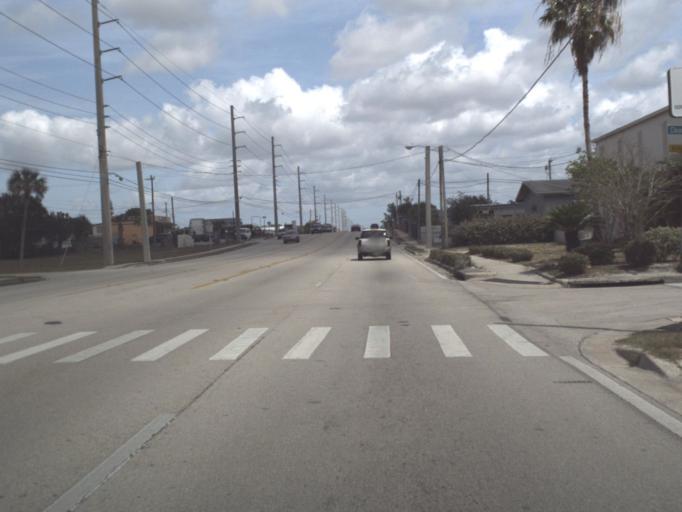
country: US
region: Florida
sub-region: Brevard County
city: Cocoa
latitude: 28.3755
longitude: -80.7550
